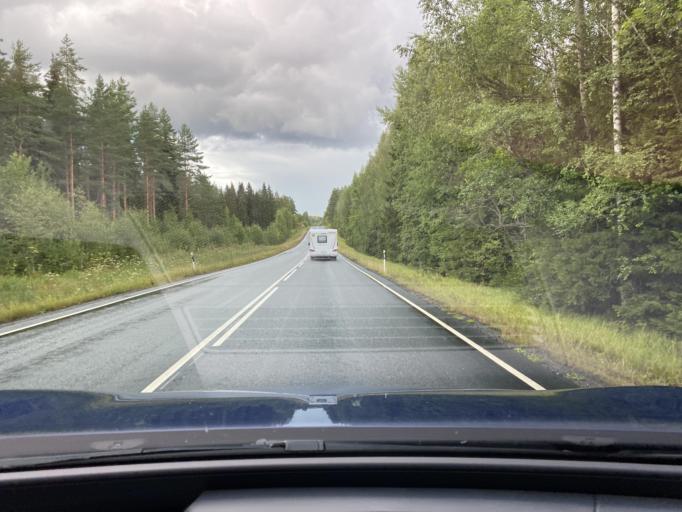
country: FI
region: Pirkanmaa
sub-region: Lounais-Pirkanmaa
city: Mouhijaervi
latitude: 61.5254
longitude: 23.0933
